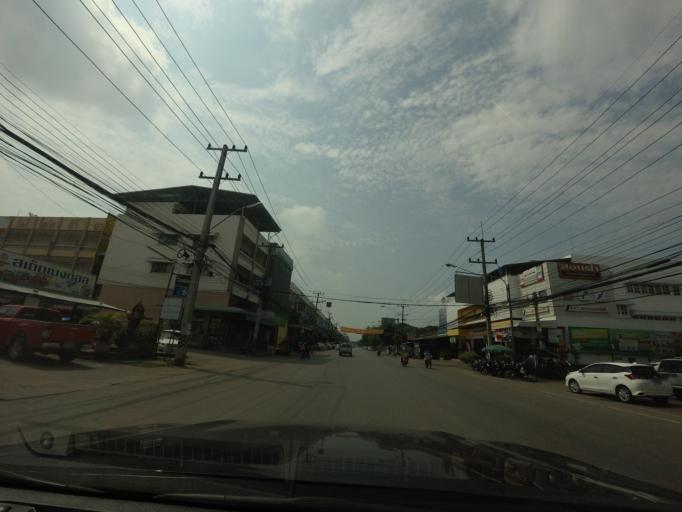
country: TH
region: Phrae
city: Phrae
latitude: 18.1357
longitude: 100.1466
